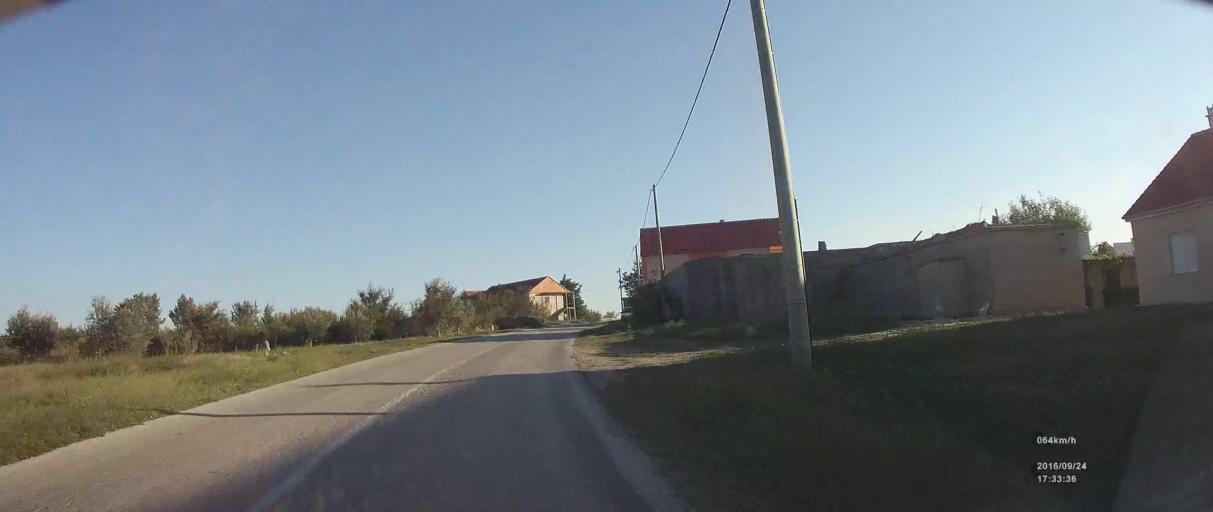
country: HR
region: Zadarska
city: Posedarje
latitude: 44.1729
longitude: 15.4576
